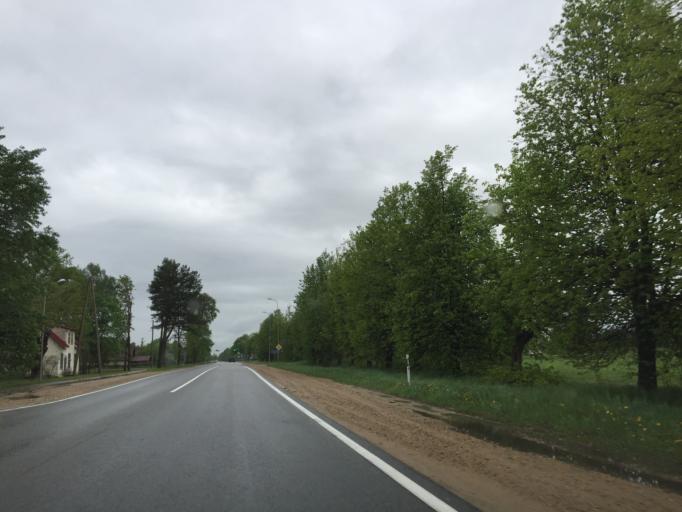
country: LV
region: Ogre
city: Ogre
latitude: 56.7782
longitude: 24.6547
